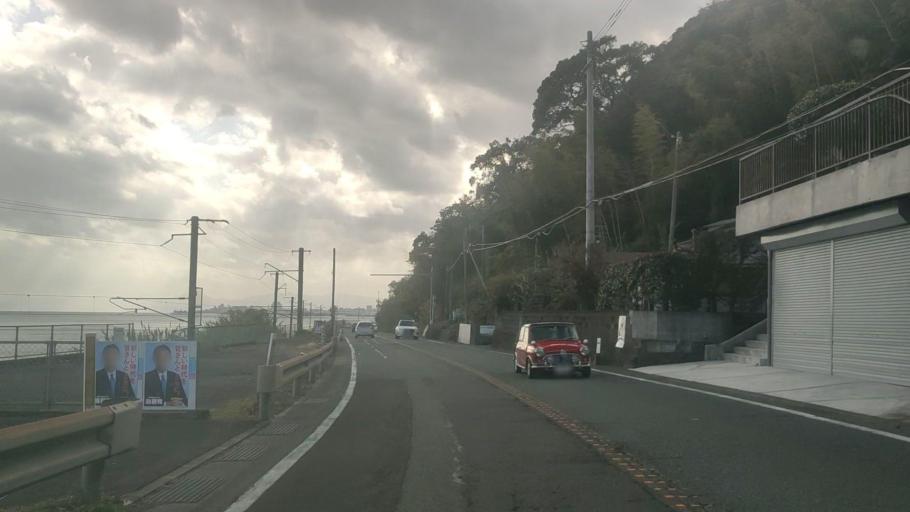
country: JP
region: Kagoshima
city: Kagoshima-shi
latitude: 31.6224
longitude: 130.5859
